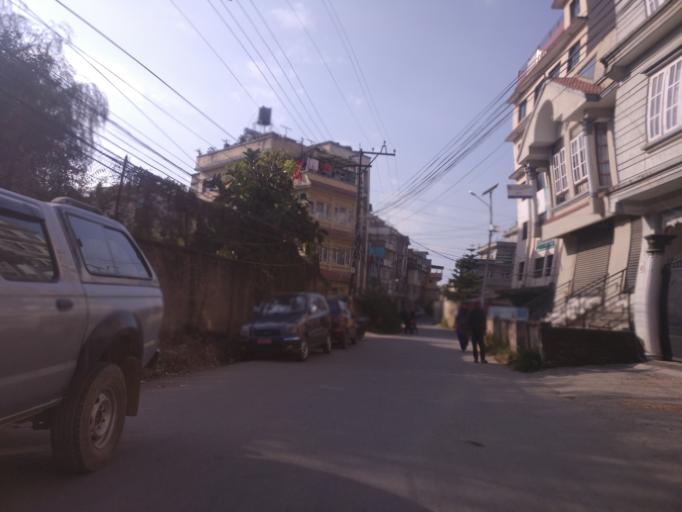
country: NP
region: Central Region
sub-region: Bagmati Zone
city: Patan
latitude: 27.6845
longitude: 85.3227
